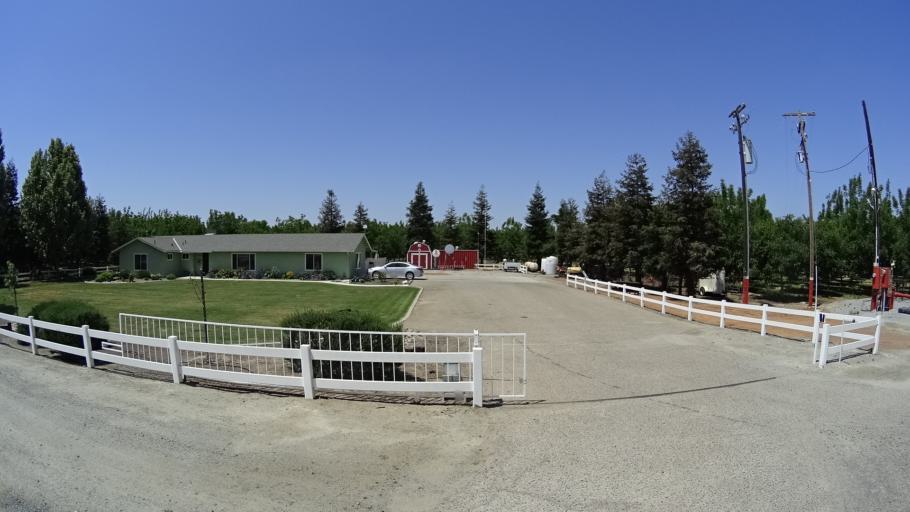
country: US
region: California
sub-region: Kings County
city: Armona
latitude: 36.3019
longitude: -119.7272
